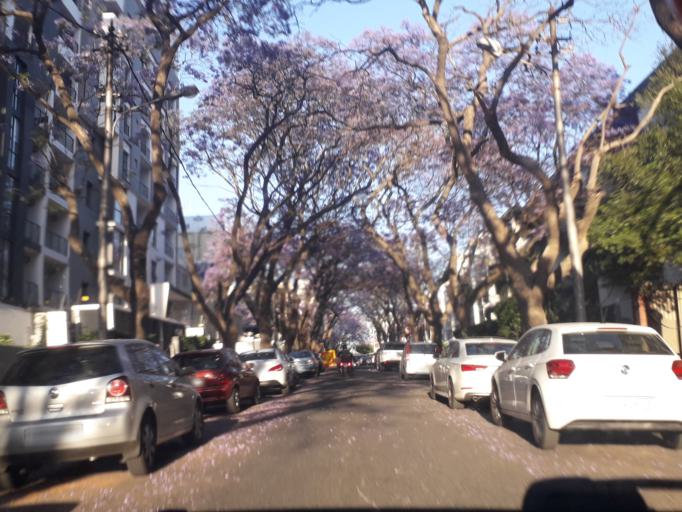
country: ZA
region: Gauteng
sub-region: City of Johannesburg Metropolitan Municipality
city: Johannesburg
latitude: -26.1453
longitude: 28.0406
